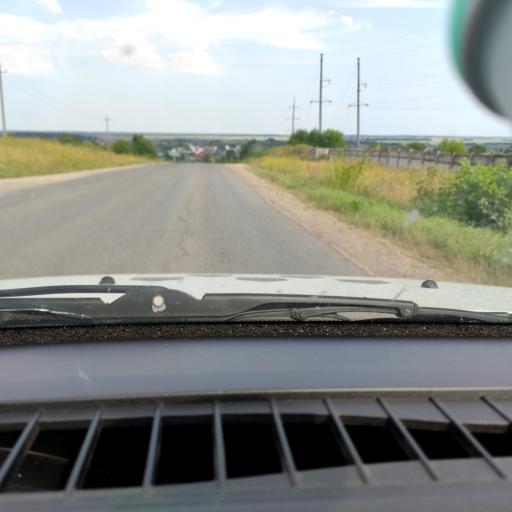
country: RU
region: Perm
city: Orda
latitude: 57.1884
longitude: 56.8818
